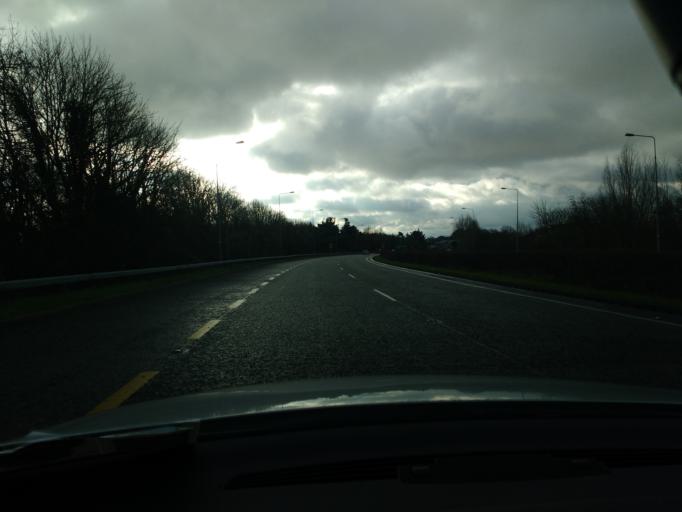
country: IE
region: Munster
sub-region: An Clar
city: Shannon
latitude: 52.7066
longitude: -8.8898
